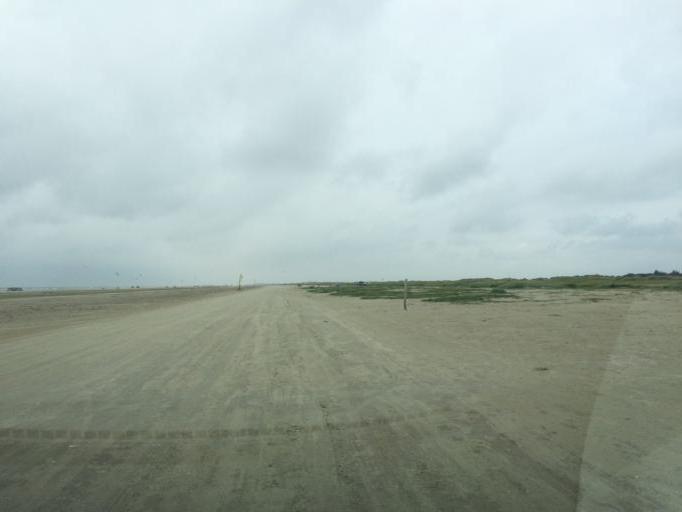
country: DK
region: South Denmark
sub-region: Fano Kommune
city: Nordby
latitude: 55.3867
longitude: 8.4020
